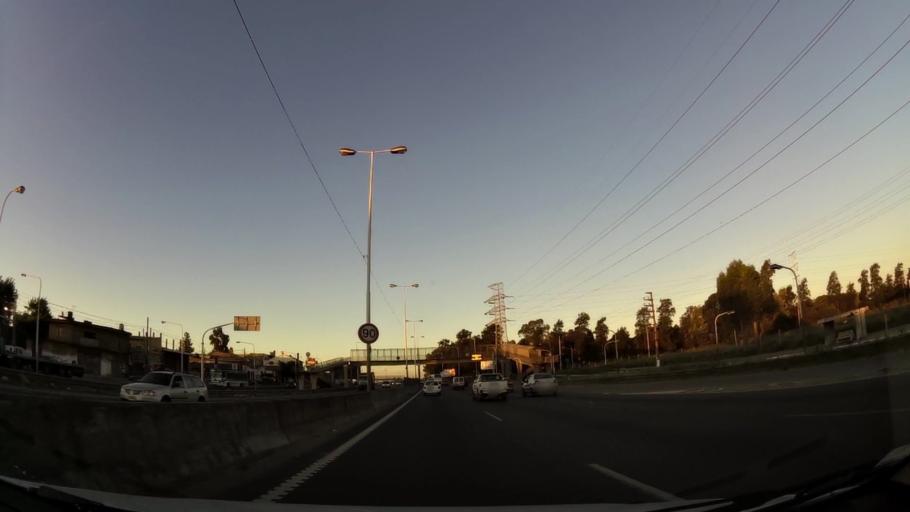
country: AR
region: Buenos Aires
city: Pontevedra
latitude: -34.7667
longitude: -58.6181
